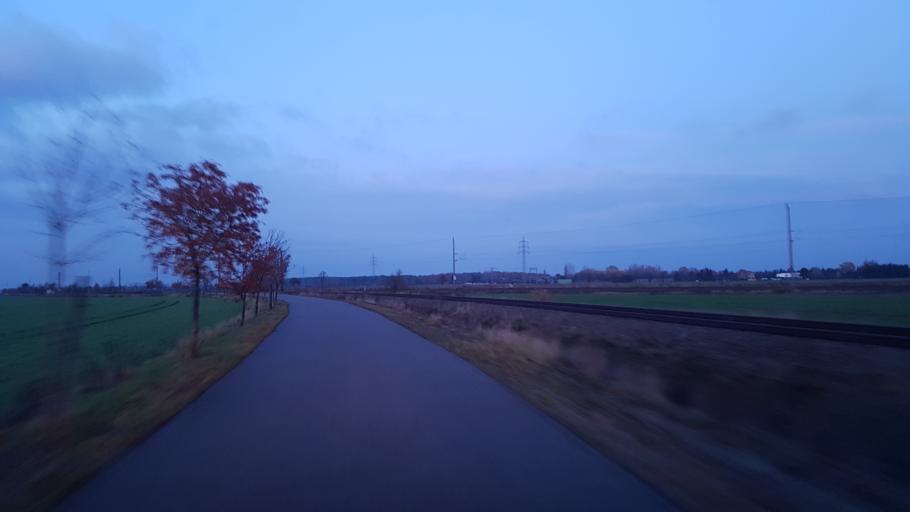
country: DE
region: Brandenburg
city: Falkenberg
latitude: 51.6299
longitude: 13.2248
